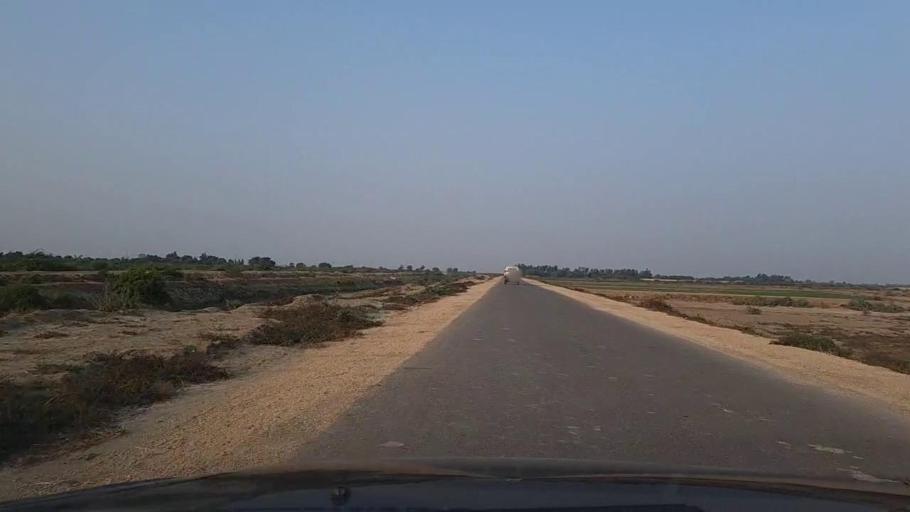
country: PK
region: Sindh
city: Mirpur Sakro
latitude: 24.4493
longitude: 67.7903
